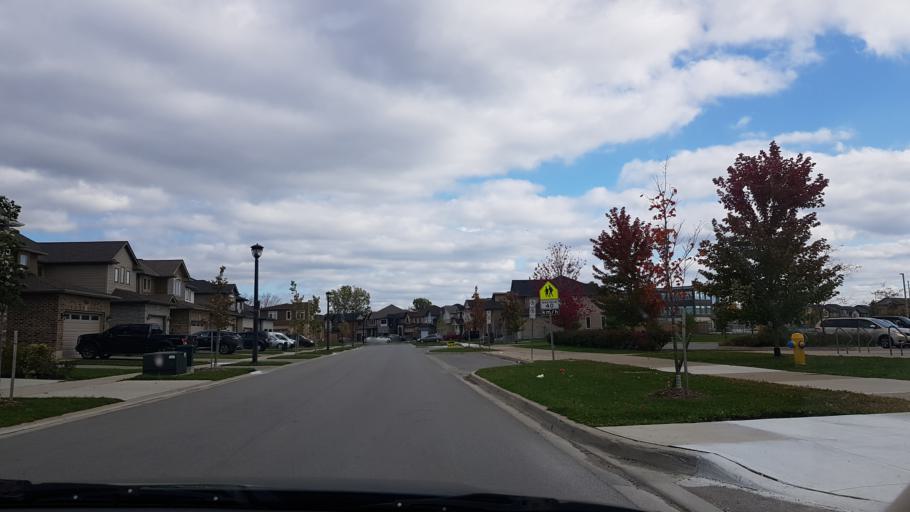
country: CA
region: Ontario
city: London
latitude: 43.0157
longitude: -81.3287
